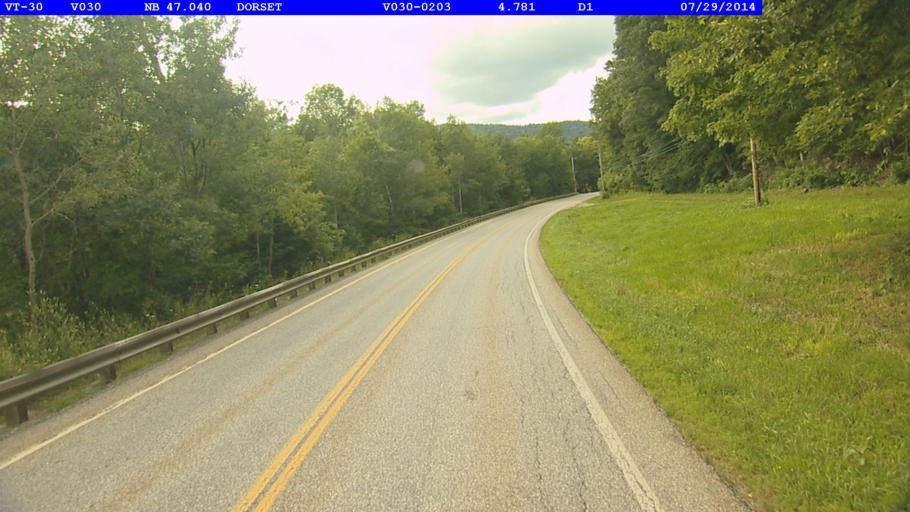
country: US
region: Vermont
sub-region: Bennington County
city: Manchester Center
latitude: 43.2688
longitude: -73.1150
